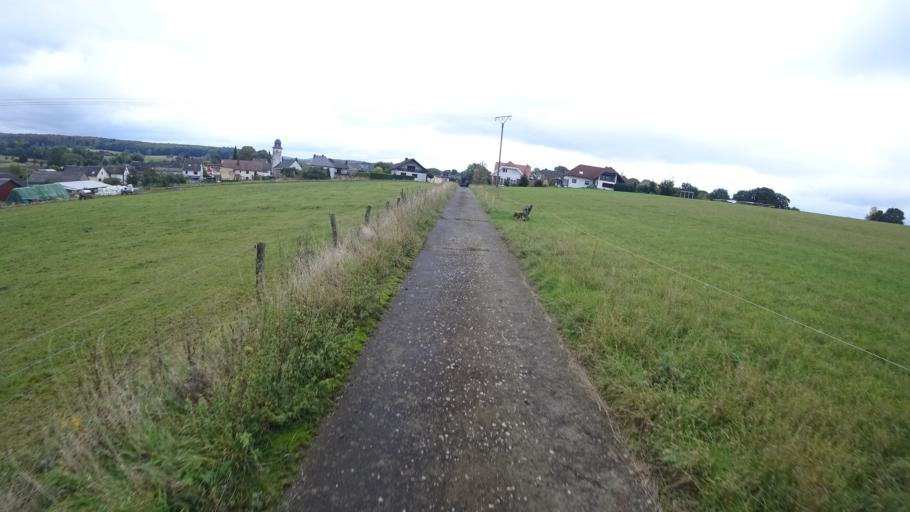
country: DE
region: Rheinland-Pfalz
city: Nordhofen
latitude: 50.5173
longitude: 7.7480
